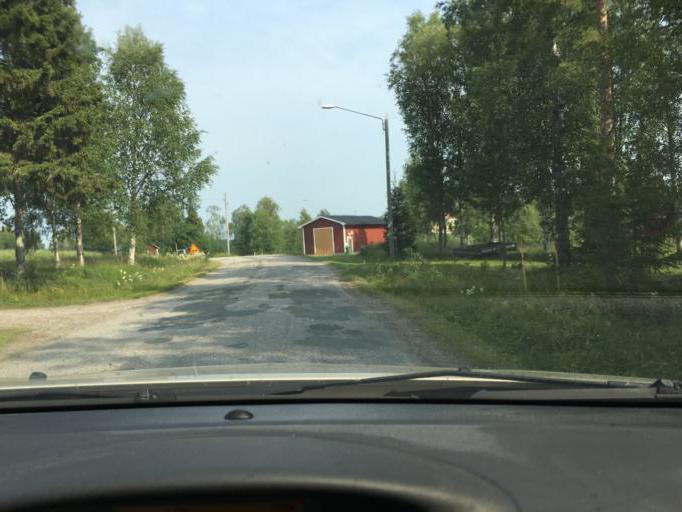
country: SE
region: Norrbotten
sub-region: Kalix Kommun
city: Rolfs
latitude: 65.7695
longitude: 23.0172
